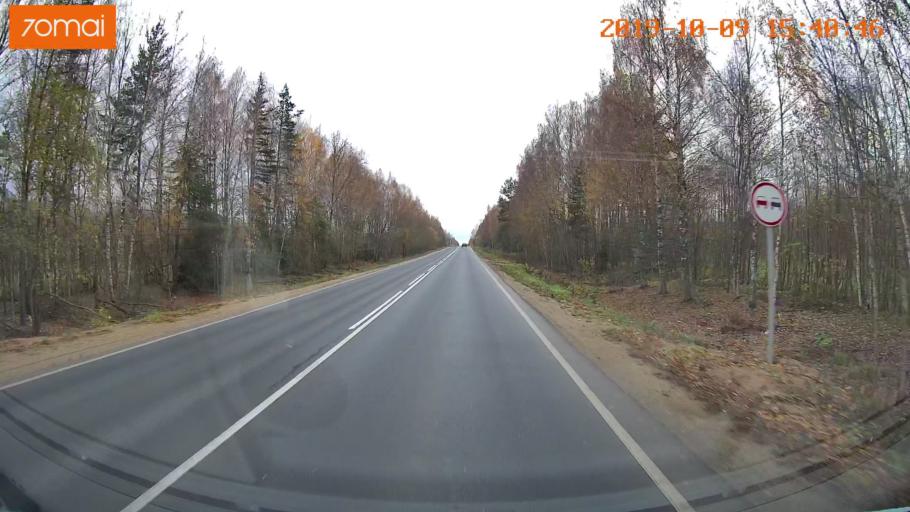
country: RU
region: Kostroma
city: Oktyabr'skiy
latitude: 57.8845
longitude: 41.1378
